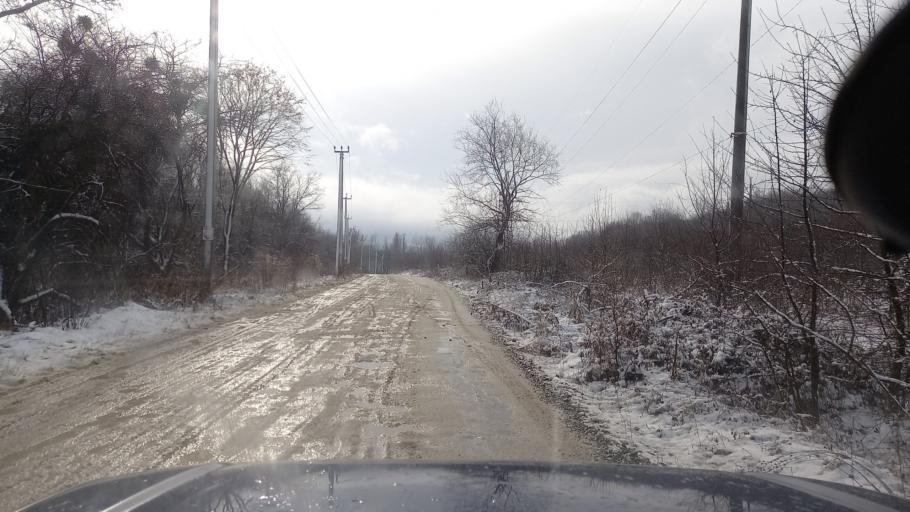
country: RU
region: Adygeya
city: Kamennomostskiy
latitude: 44.2445
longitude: 40.1983
